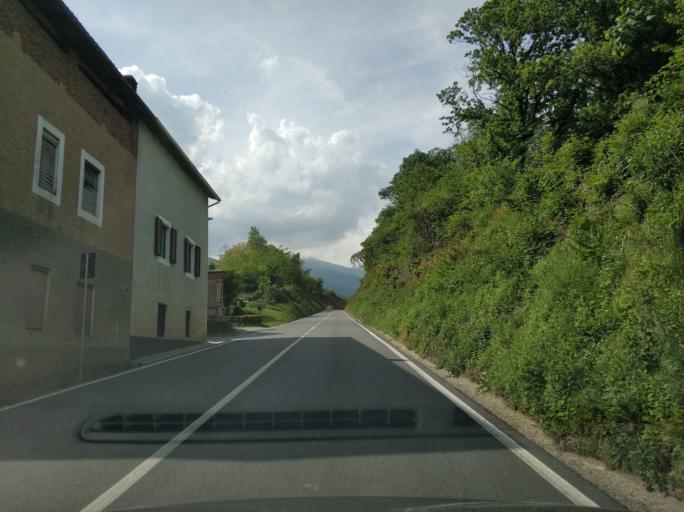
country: IT
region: Piedmont
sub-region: Provincia di Torino
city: Corio
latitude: 45.3022
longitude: 7.5412
